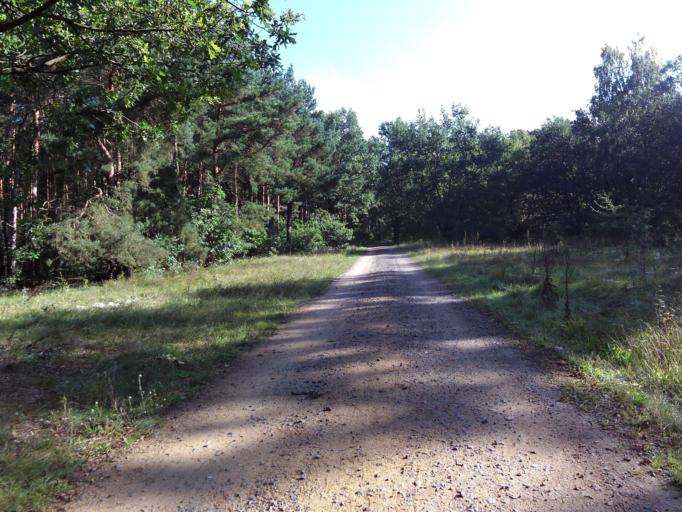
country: DE
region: Saxony-Anhalt
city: Coswig
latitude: 51.8746
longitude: 12.4796
